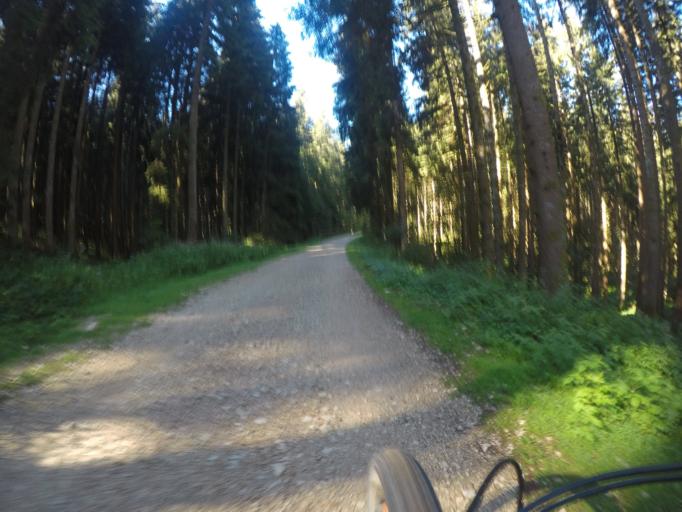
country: IT
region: Veneto
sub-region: Provincia di Vicenza
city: Canove di Roana
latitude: 45.8471
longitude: 11.4707
